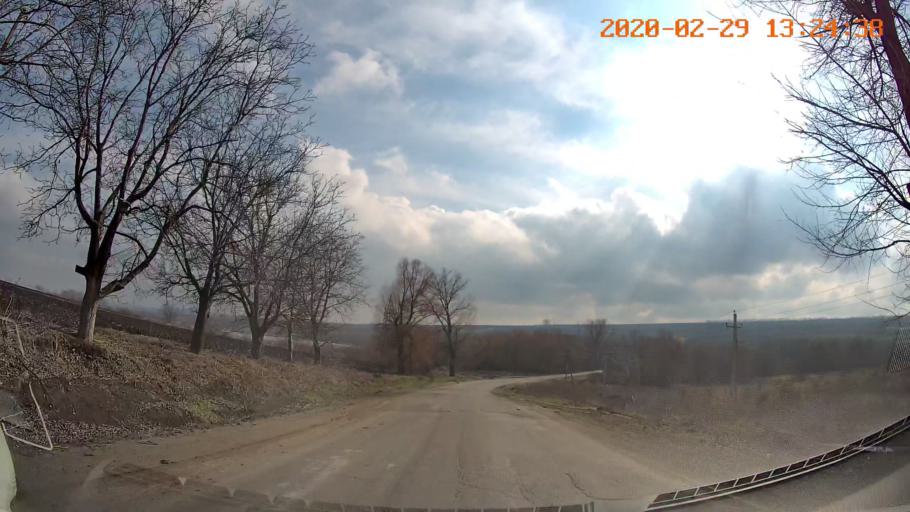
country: MD
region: Telenesti
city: Camenca
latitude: 47.9368
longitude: 28.6284
